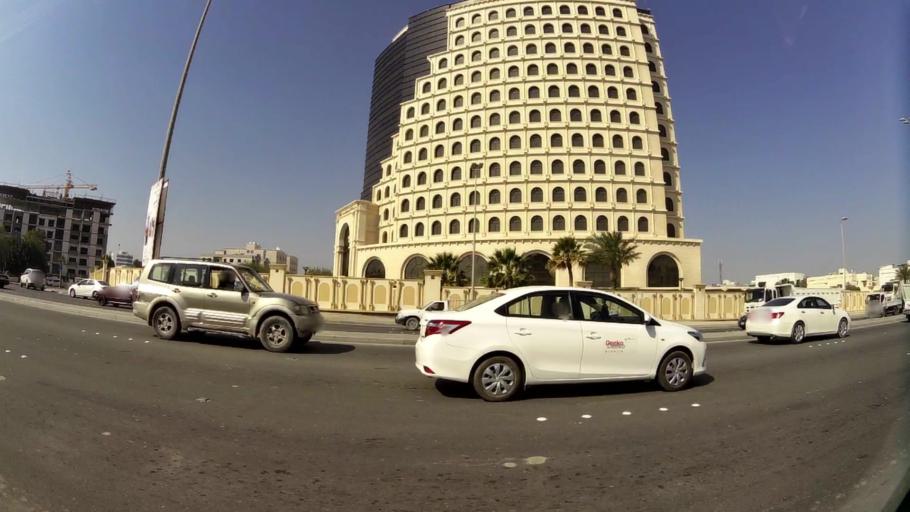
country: BH
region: Manama
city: Manama
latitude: 26.2071
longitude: 50.5989
